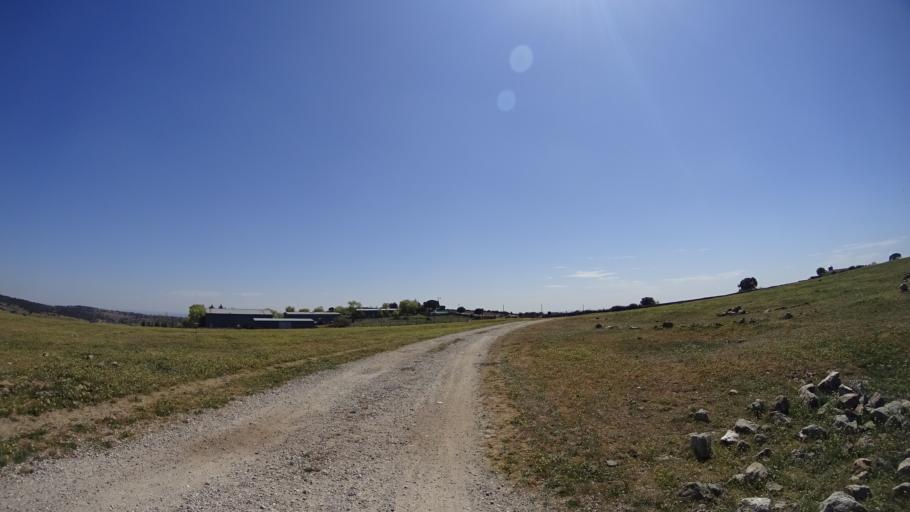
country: ES
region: Madrid
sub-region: Provincia de Madrid
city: Colmenar Viejo
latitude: 40.6904
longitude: -3.7557
